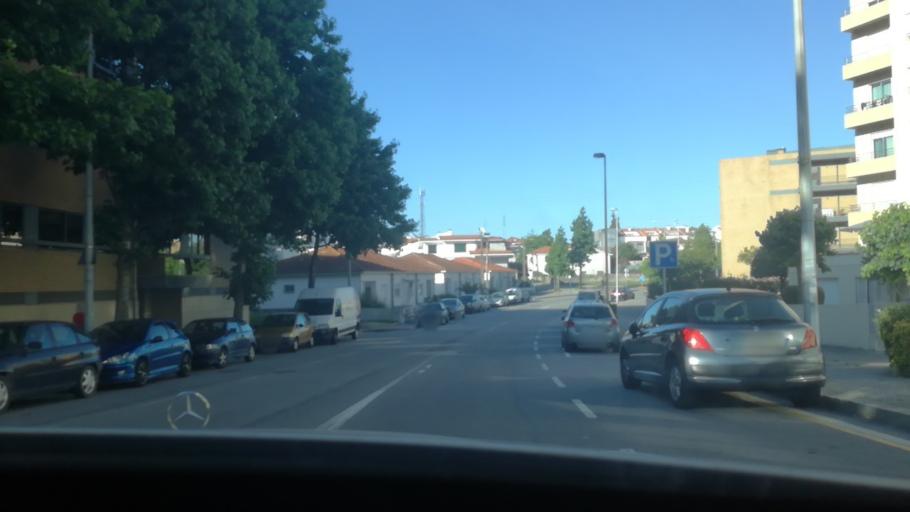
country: PT
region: Porto
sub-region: Maia
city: Maia
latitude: 41.2309
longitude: -8.6130
